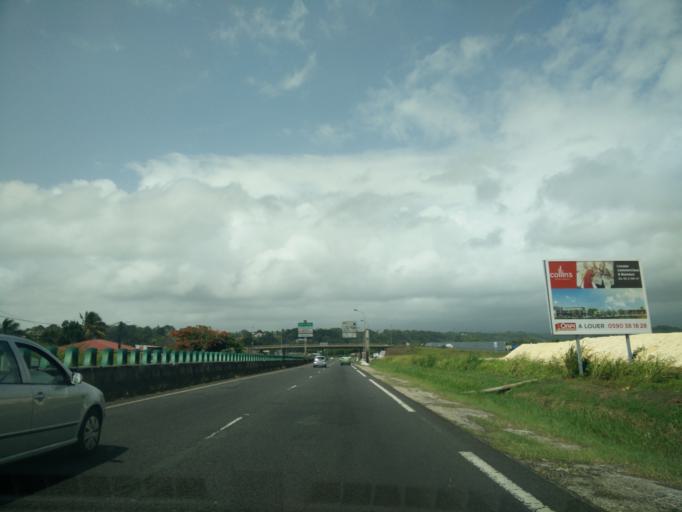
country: GP
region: Guadeloupe
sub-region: Guadeloupe
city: Petit-Bourg
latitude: 16.2043
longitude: -61.6050
